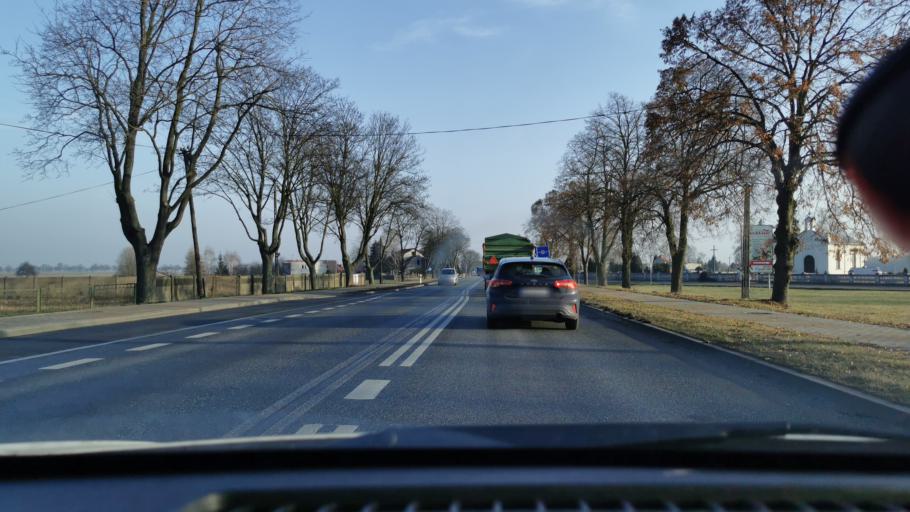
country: PL
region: Lodz Voivodeship
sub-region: Powiat sieradzki
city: Wroblew
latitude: 51.6105
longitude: 18.6194
